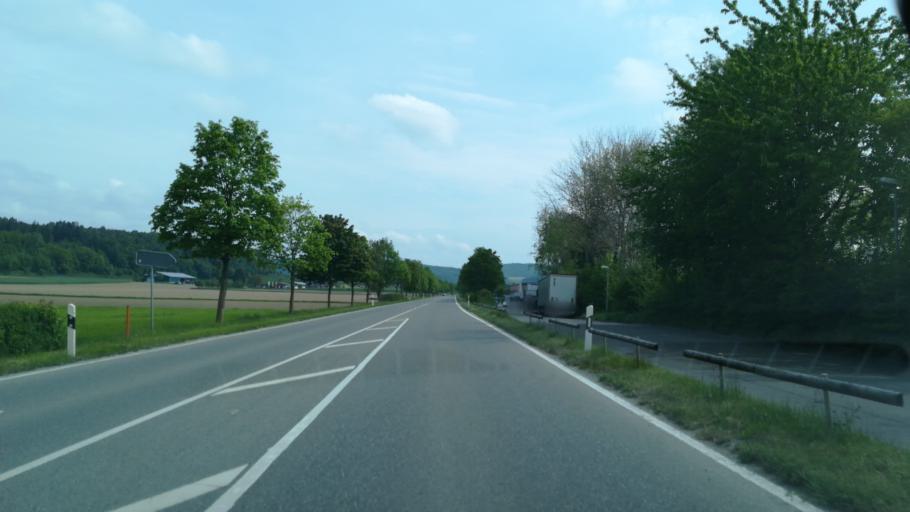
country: DE
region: Baden-Wuerttemberg
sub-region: Freiburg Region
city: Steisslingen
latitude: 47.7793
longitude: 8.9084
